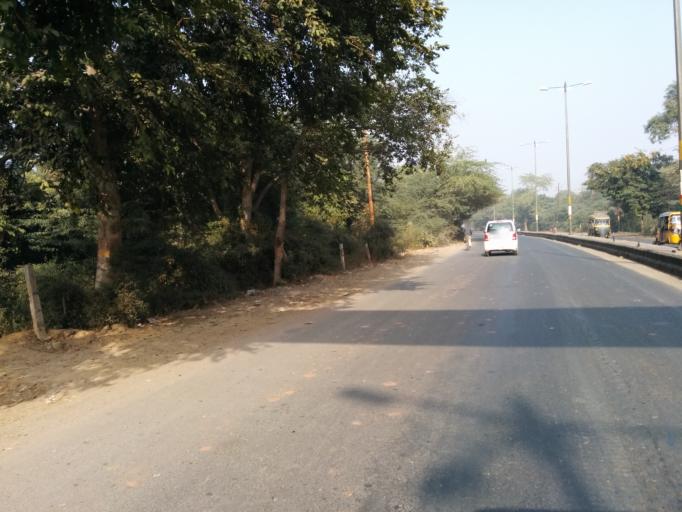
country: IN
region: Uttar Pradesh
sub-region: Mathura
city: Vrindavan
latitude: 27.5615
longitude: 77.6830
